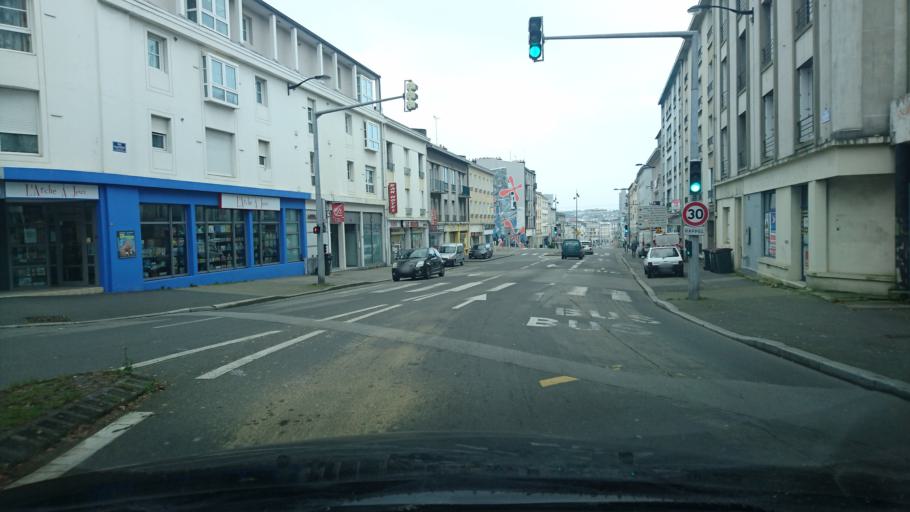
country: FR
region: Brittany
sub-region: Departement du Finistere
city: Brest
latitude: 48.3839
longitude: -4.5050
